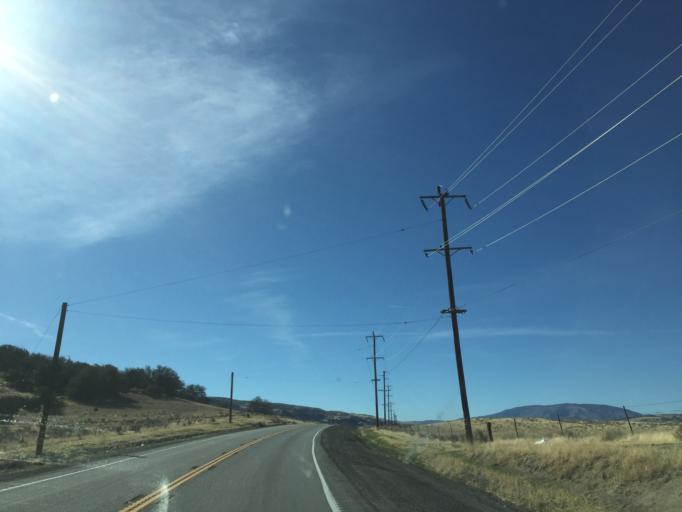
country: US
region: California
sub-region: Kern County
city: Lebec
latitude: 34.7752
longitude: -118.6766
